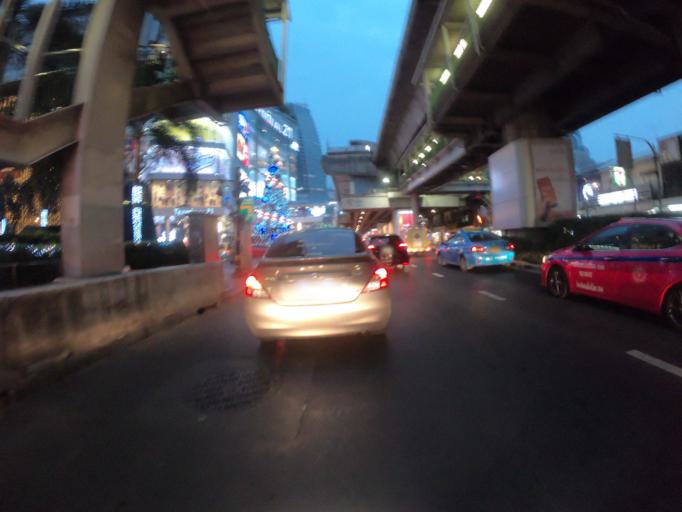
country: TH
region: Bangkok
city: Khlong Toei
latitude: 13.7378
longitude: 100.5595
